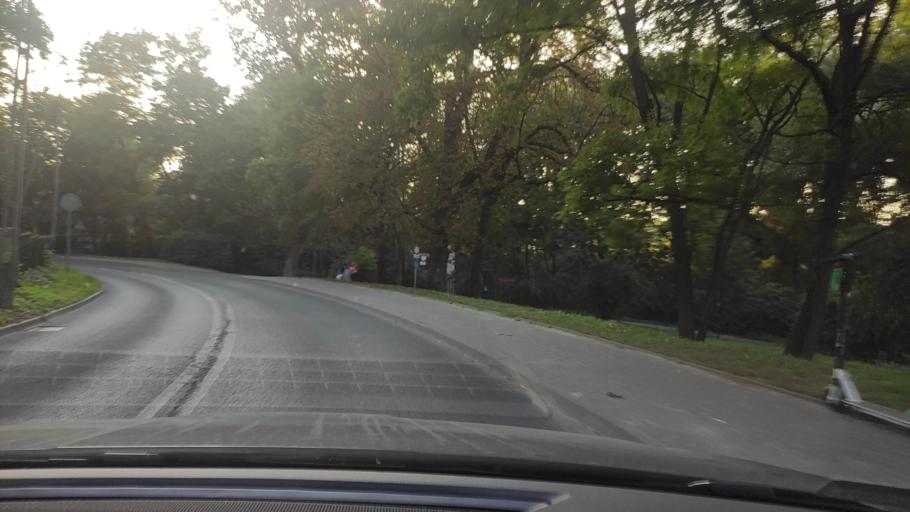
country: PL
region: Greater Poland Voivodeship
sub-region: Powiat poznanski
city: Swarzedz
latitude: 52.4136
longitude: 17.0751
